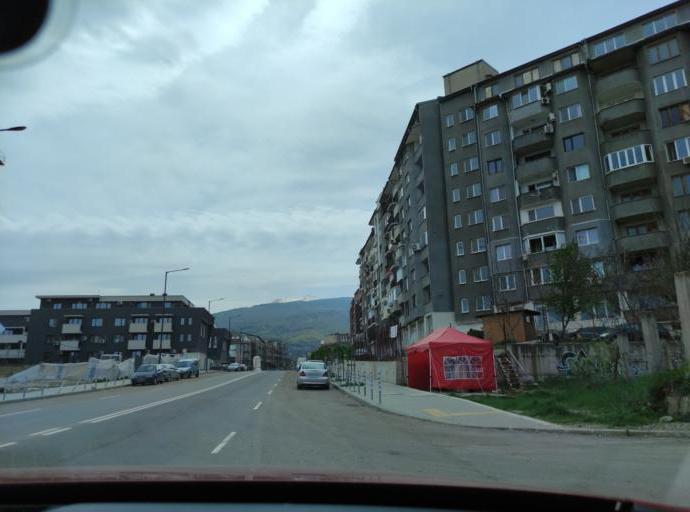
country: BG
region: Sofia-Capital
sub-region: Stolichna Obshtina
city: Sofia
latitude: 42.6379
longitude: 23.3417
